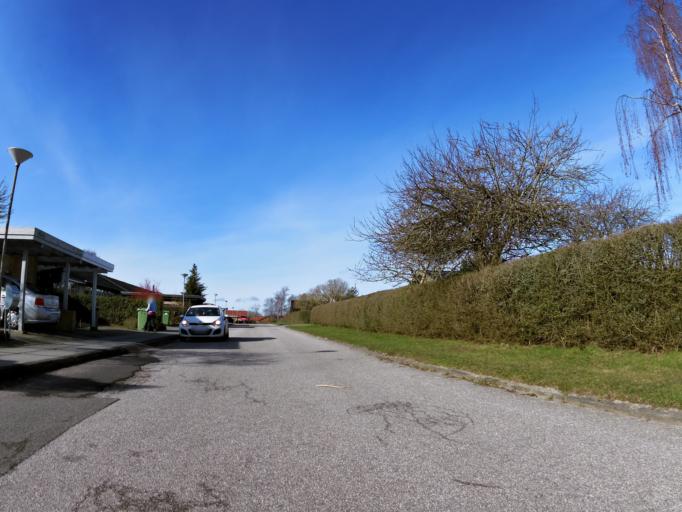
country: DK
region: Central Jutland
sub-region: Arhus Kommune
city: Tranbjerg
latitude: 56.0872
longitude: 10.1183
